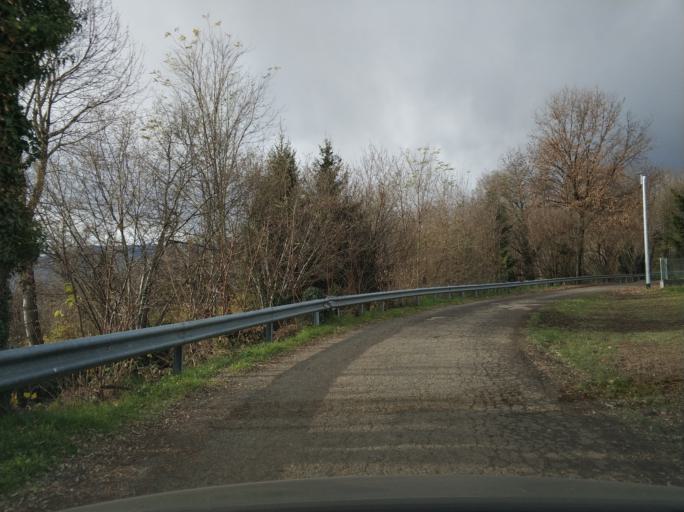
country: IT
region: Piedmont
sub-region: Provincia di Torino
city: Cirie
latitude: 45.2240
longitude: 7.5814
